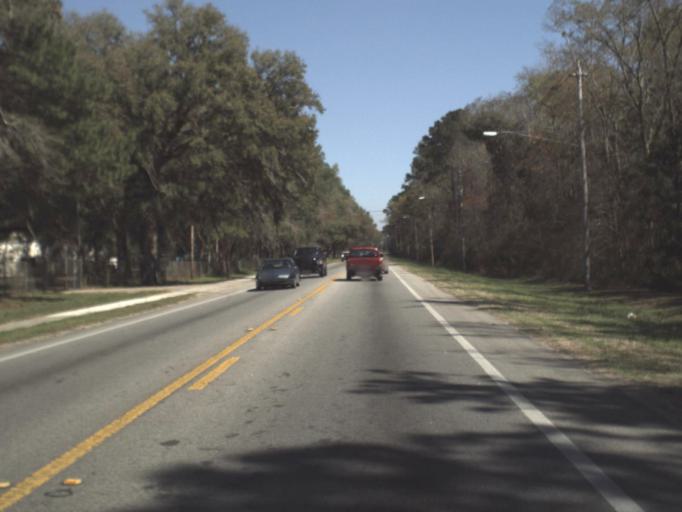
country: US
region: Florida
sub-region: Leon County
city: Tallahassee
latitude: 30.4126
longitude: -84.3241
